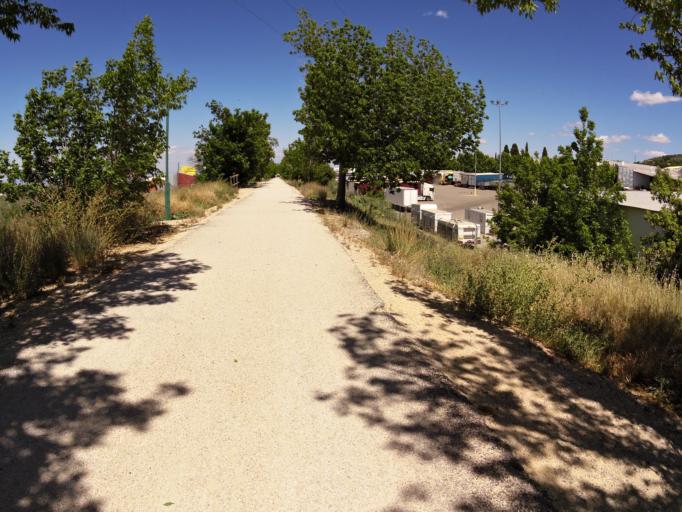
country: ES
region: Andalusia
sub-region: Provincia de Jaen
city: Torre del Campo
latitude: 37.7767
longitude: -3.8996
